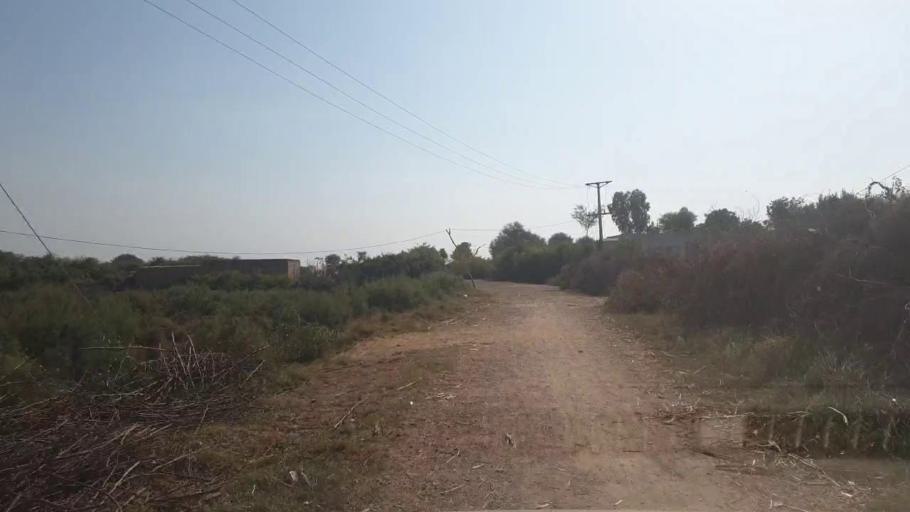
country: PK
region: Sindh
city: Chambar
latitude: 25.3196
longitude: 68.8655
